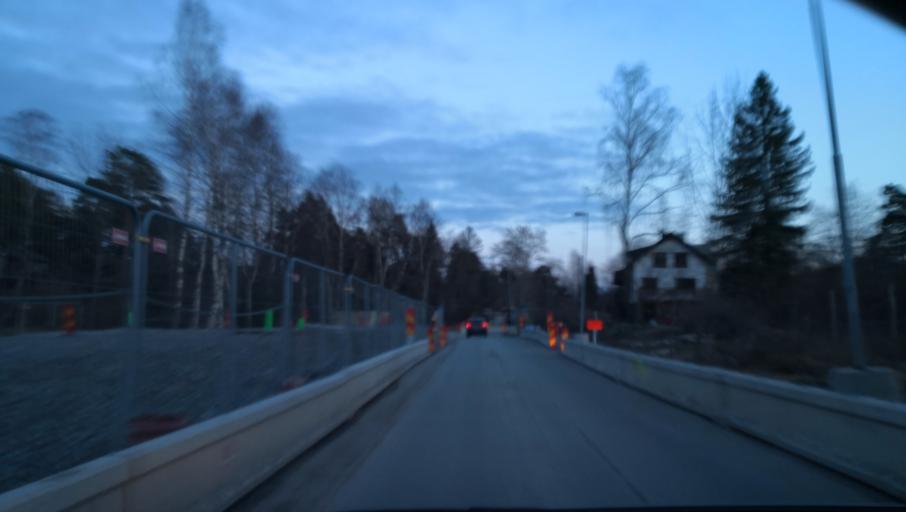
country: SE
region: Stockholm
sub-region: Nacka Kommun
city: Kummelnas
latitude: 59.3460
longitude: 18.2904
